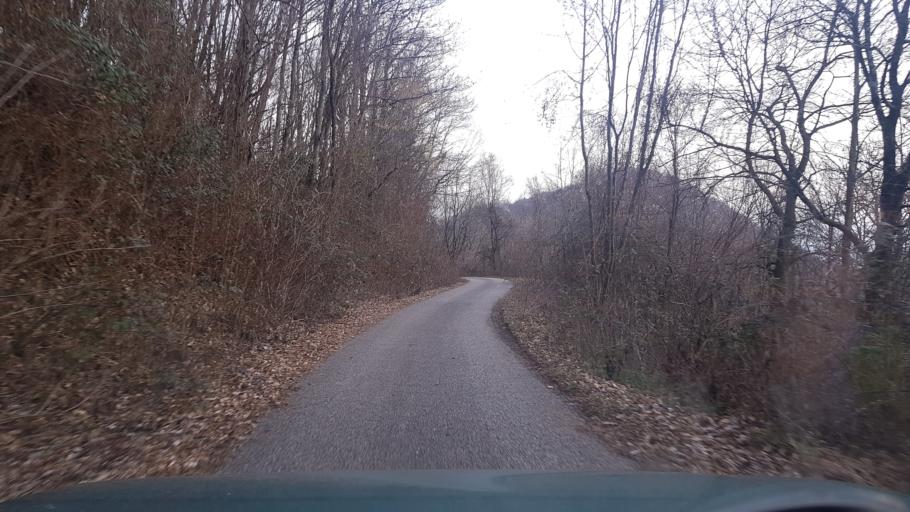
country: IT
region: Friuli Venezia Giulia
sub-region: Provincia di Udine
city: Pulfero
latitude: 46.1496
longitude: 13.4580
